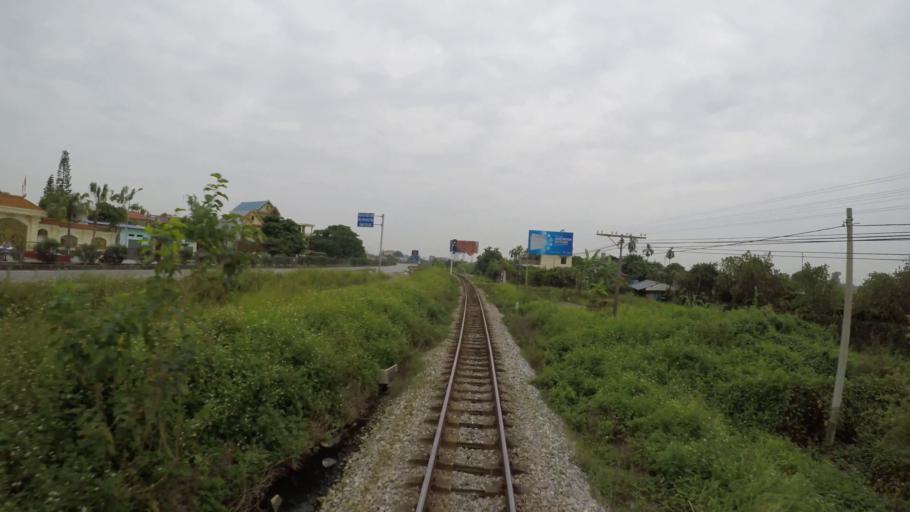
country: VN
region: Hai Duong
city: Phu Thai
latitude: 20.9353
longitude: 106.5502
